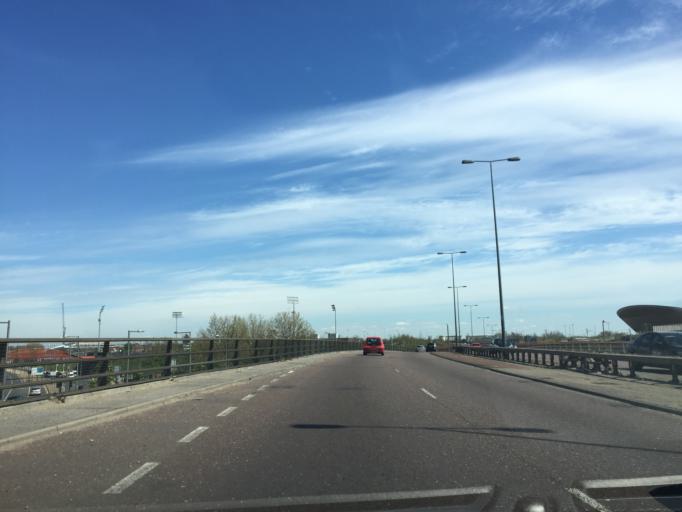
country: GB
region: England
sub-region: Greater London
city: Hackney
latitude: 51.5512
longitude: -0.0216
